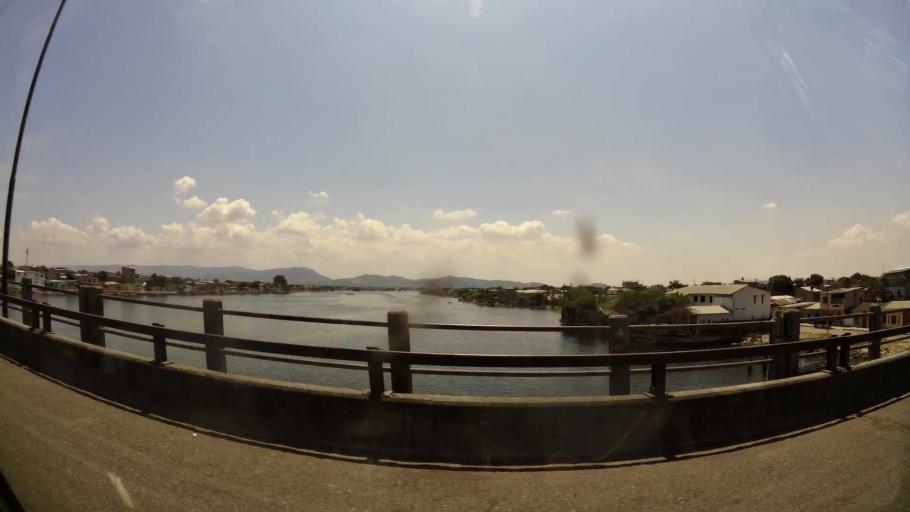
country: EC
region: Guayas
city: Guayaquil
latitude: -2.2390
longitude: -79.9123
